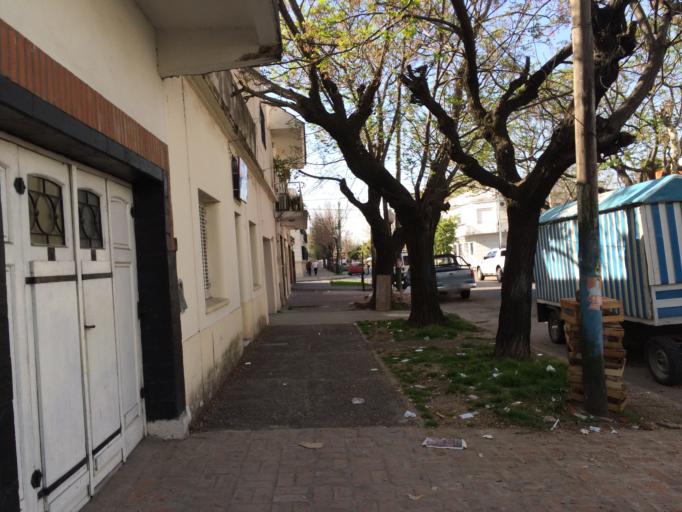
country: AR
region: Buenos Aires
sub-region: Partido de Lomas de Zamora
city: Lomas de Zamora
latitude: -34.7431
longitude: -58.3886
